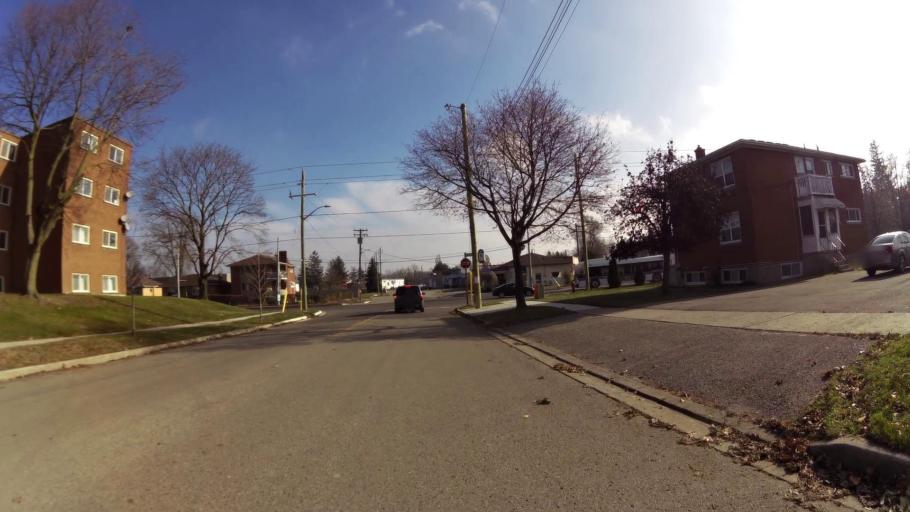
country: CA
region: Ontario
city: Kitchener
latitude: 43.4319
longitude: -80.4799
